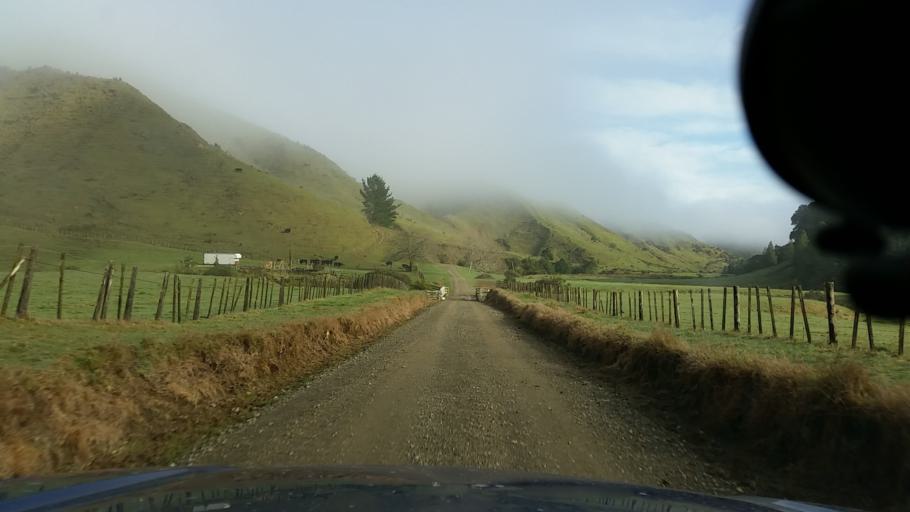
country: NZ
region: Taranaki
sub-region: New Plymouth District
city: Waitara
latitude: -38.9782
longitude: 174.7522
